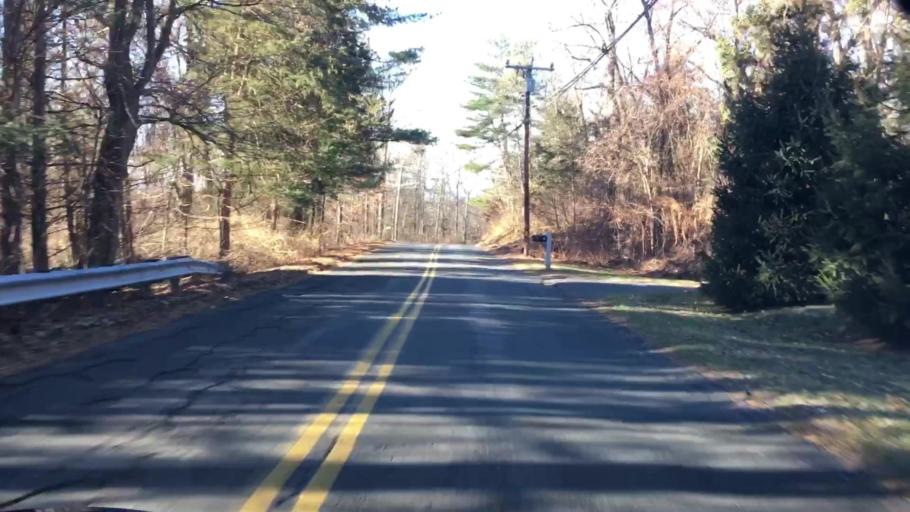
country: US
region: Connecticut
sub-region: Tolland County
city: Somers
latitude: 41.9701
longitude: -72.4384
